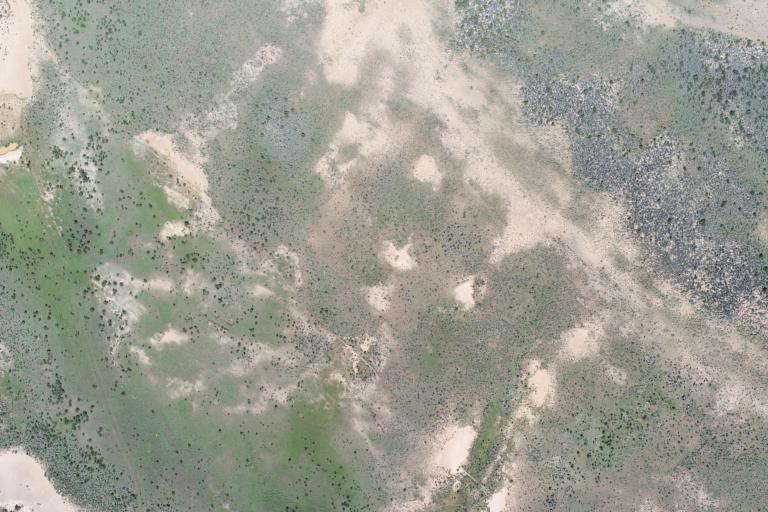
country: BO
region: La Paz
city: Curahuara de Carangas
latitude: -17.2973
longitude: -68.5220
